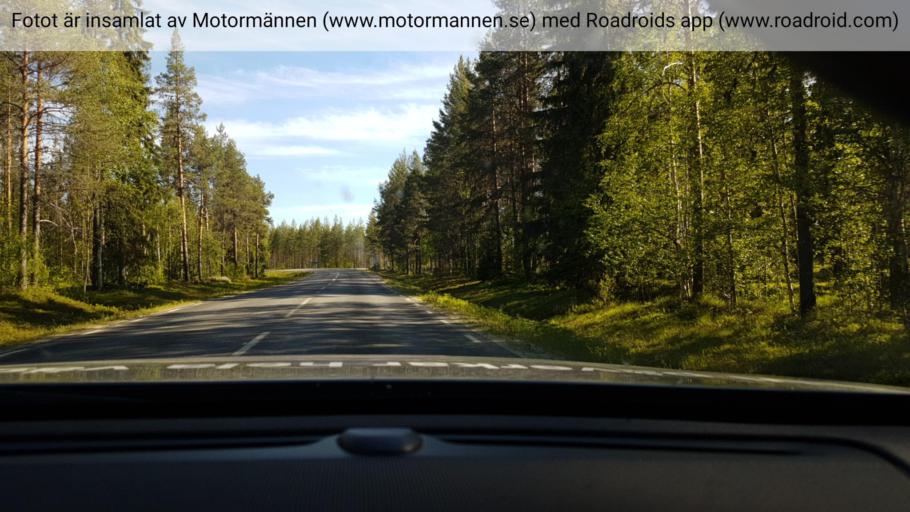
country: SE
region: Vaesterbotten
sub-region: Norsjo Kommun
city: Norsjoe
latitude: 64.7230
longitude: 19.1326
